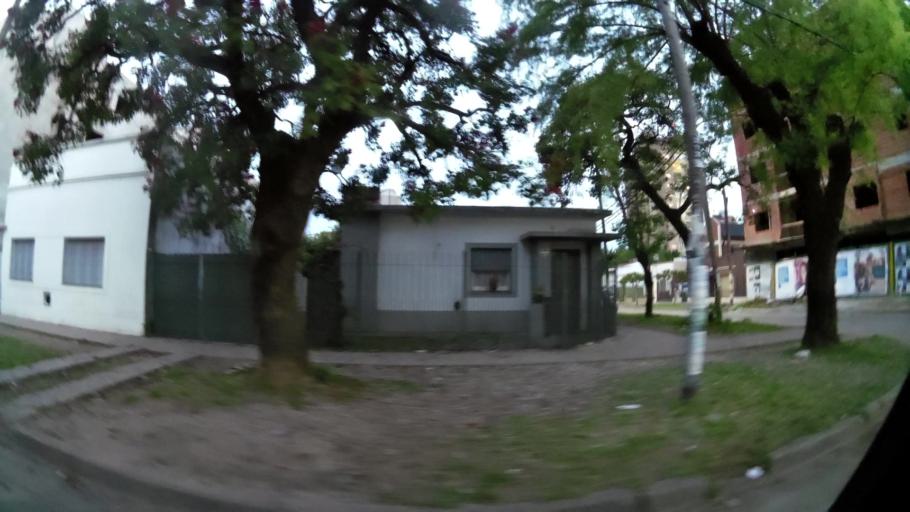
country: AR
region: Buenos Aires
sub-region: Partido de Quilmes
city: Quilmes
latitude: -34.8028
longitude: -58.2802
